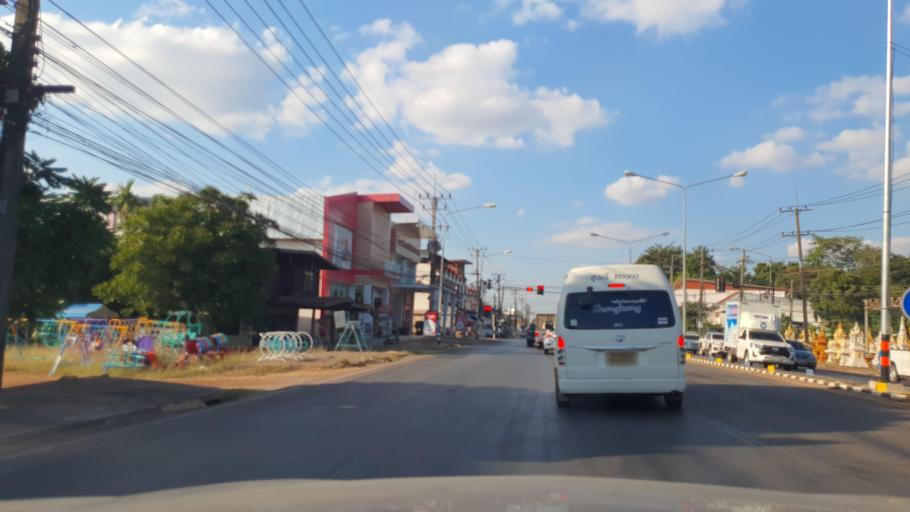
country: TH
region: Sakon Nakhon
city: Sakon Nakhon
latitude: 17.1829
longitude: 104.0942
